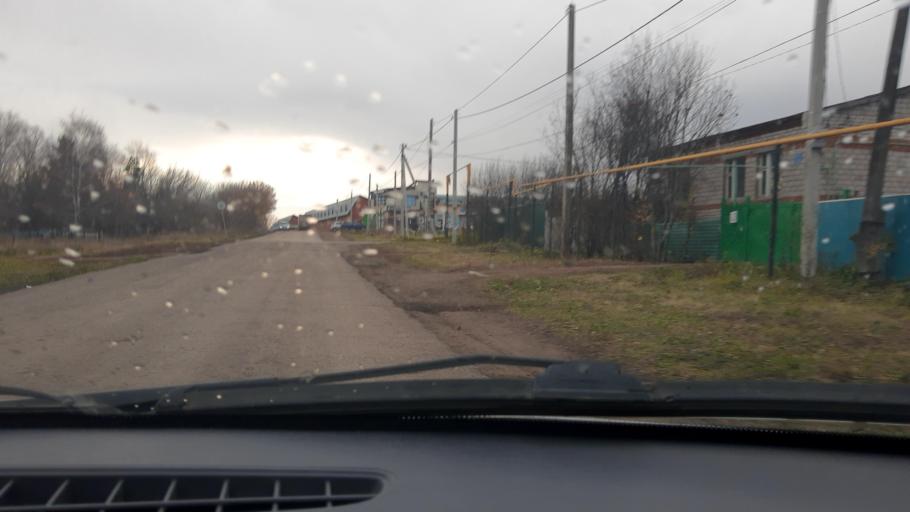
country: RU
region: Bashkortostan
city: Avdon
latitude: 54.7039
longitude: 55.8073
